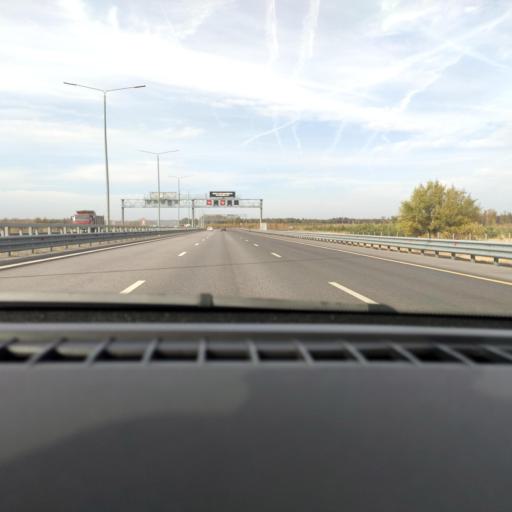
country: RU
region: Voronezj
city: Somovo
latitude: 51.7726
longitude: 39.3019
